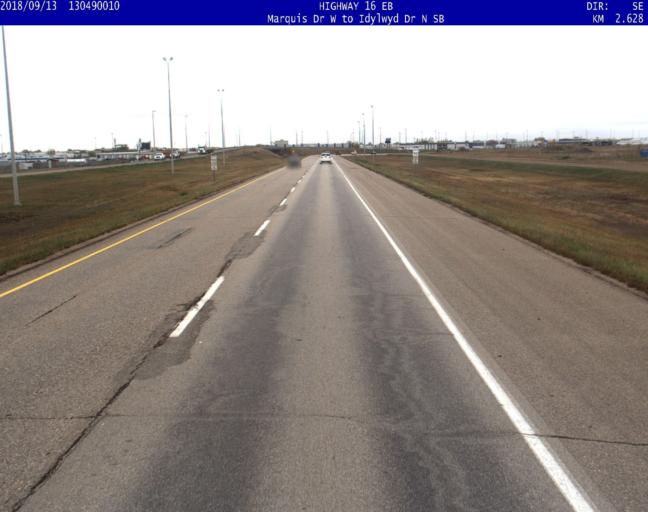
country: CA
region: Saskatchewan
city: Saskatoon
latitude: 52.1857
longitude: -106.6774
